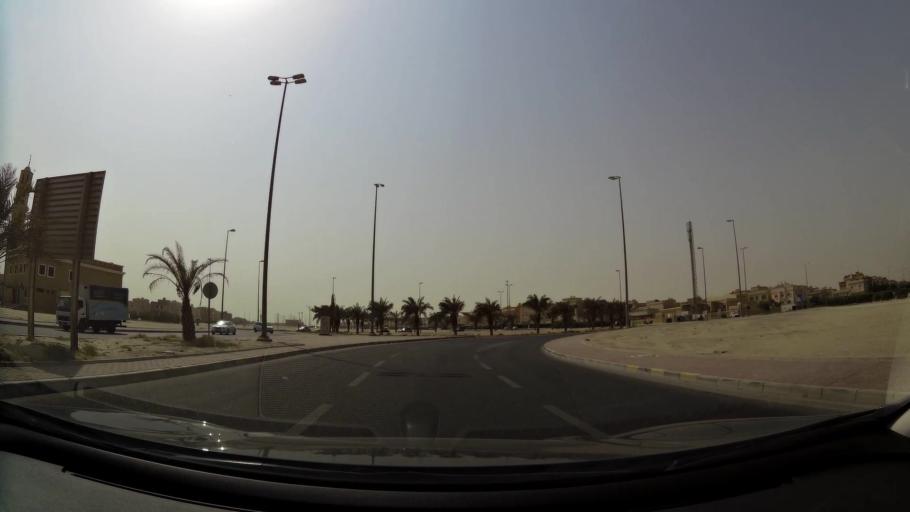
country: KW
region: Muhafazat al Jahra'
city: Al Jahra'
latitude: 29.3131
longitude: 47.7269
